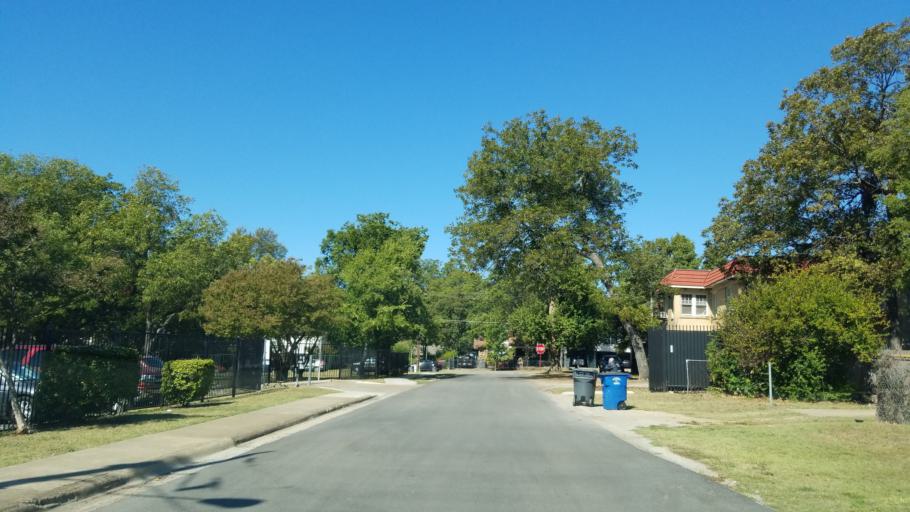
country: US
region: Texas
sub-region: Dallas County
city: Highland Park
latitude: 32.8041
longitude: -96.7535
